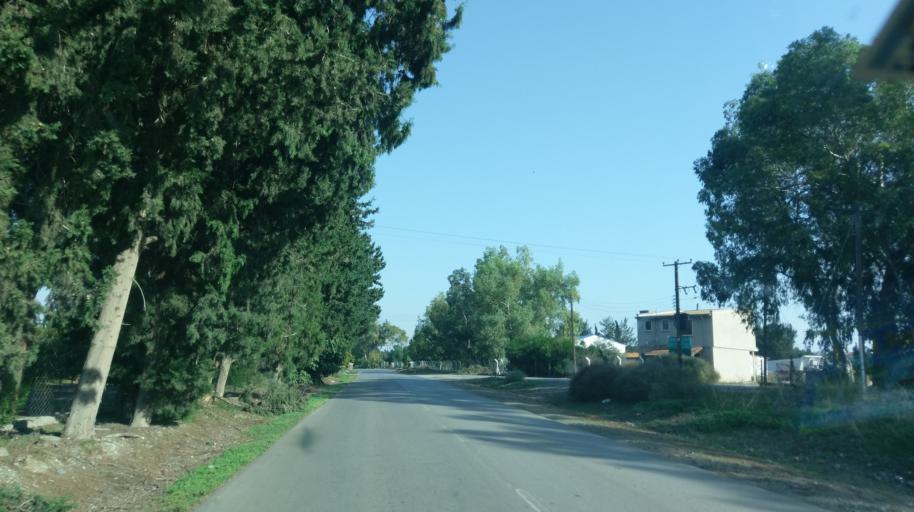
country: CY
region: Lefkosia
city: Morfou
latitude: 35.1901
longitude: 32.9723
